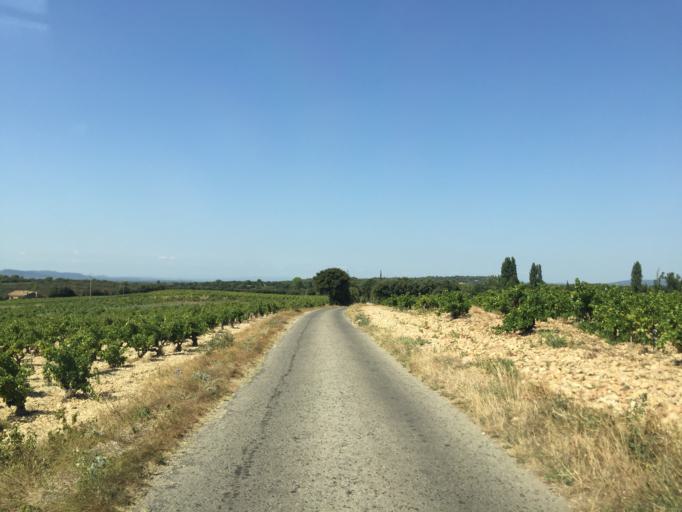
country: FR
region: Provence-Alpes-Cote d'Azur
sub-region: Departement du Vaucluse
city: Orange
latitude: 44.1045
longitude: 4.8197
